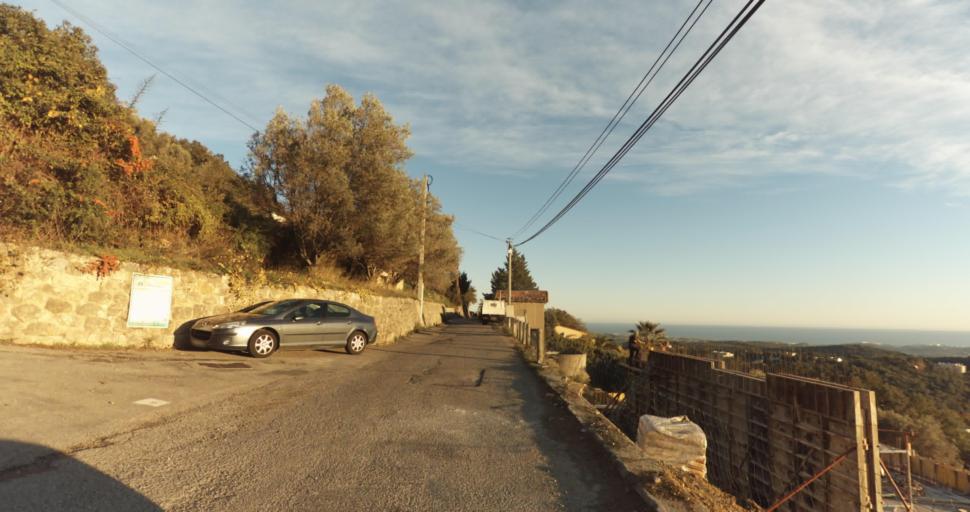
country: FR
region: Provence-Alpes-Cote d'Azur
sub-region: Departement des Alpes-Maritimes
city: Vence
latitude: 43.7295
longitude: 7.0970
